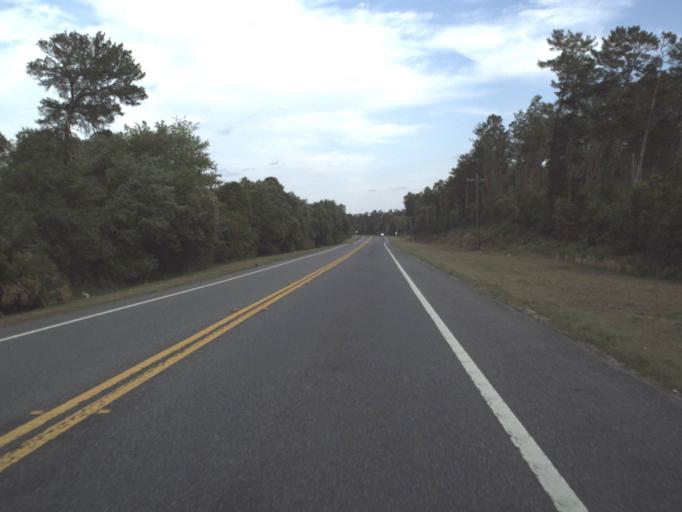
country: US
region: Florida
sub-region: Lake County
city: Astor
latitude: 29.1760
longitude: -81.6991
